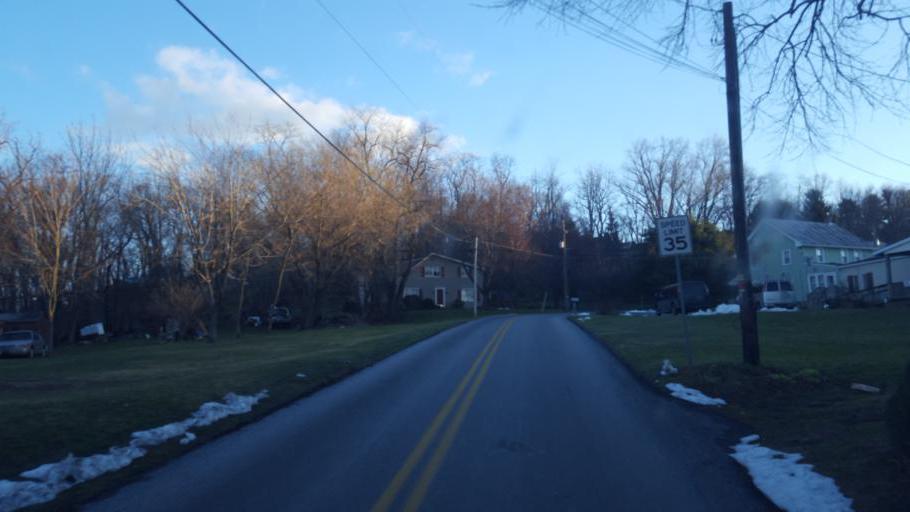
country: US
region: Pennsylvania
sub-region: Lancaster County
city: New Holland
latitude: 40.0733
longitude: -76.0844
